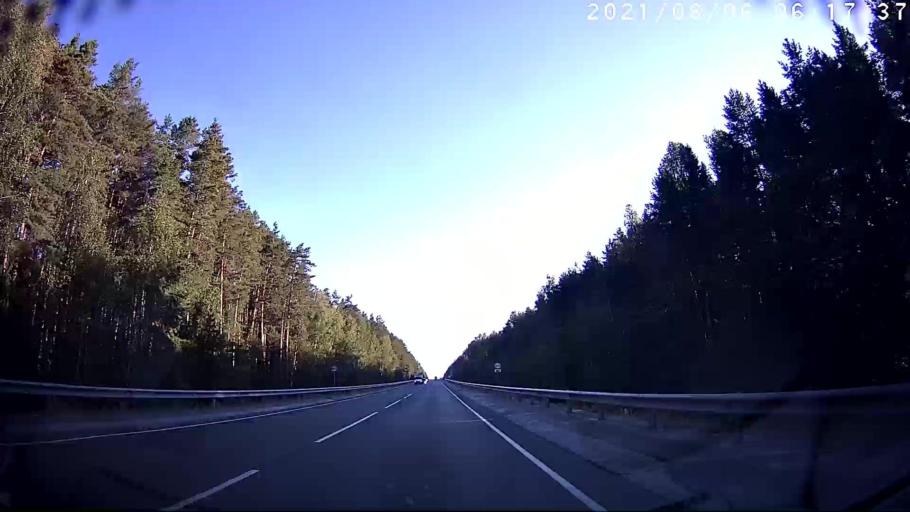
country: RU
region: Mariy-El
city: Pomary
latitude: 56.0159
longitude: 48.3801
